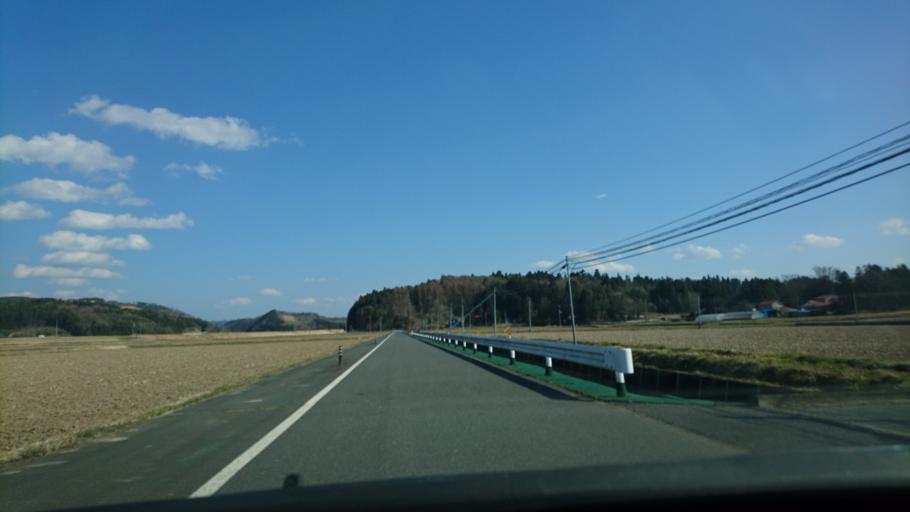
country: JP
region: Iwate
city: Ichinoseki
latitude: 38.8130
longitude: 141.2049
